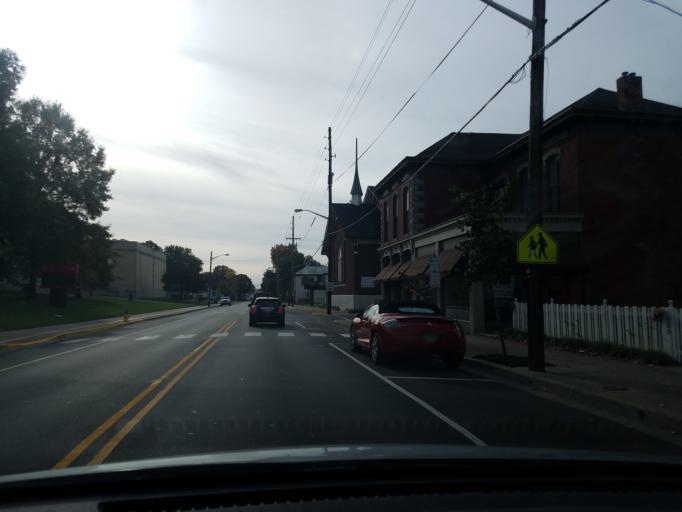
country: US
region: Indiana
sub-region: Floyd County
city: New Albany
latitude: 38.2981
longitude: -85.8119
